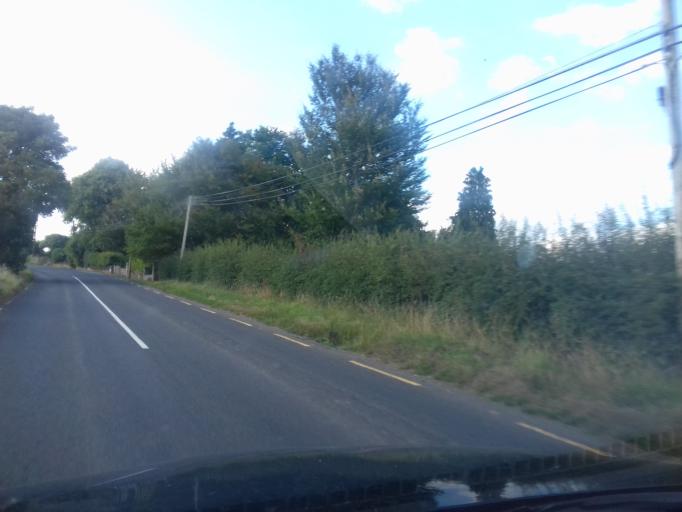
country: IE
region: Leinster
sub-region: Loch Garman
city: New Ross
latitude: 52.4432
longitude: -6.9613
